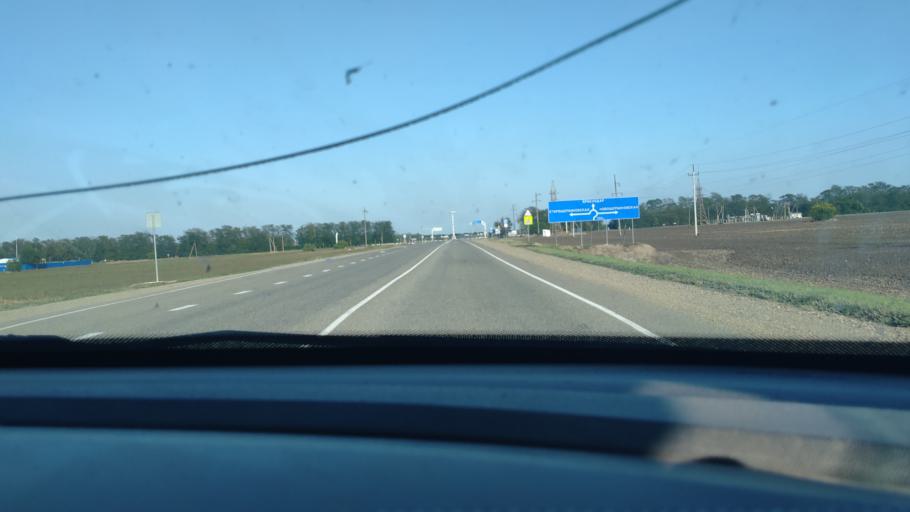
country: RU
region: Krasnodarskiy
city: Staroshcherbinovskaya
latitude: 46.6105
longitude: 38.6505
